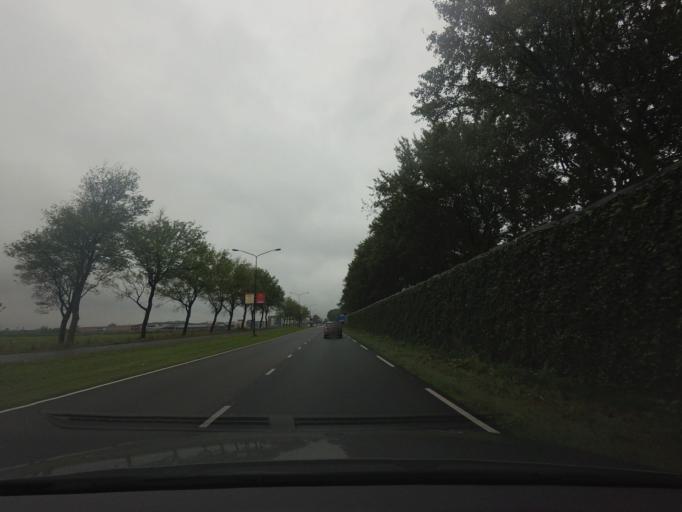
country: NL
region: North Holland
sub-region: Gemeente Langedijk
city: Broek op Langedijk
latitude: 52.6578
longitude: 4.8067
